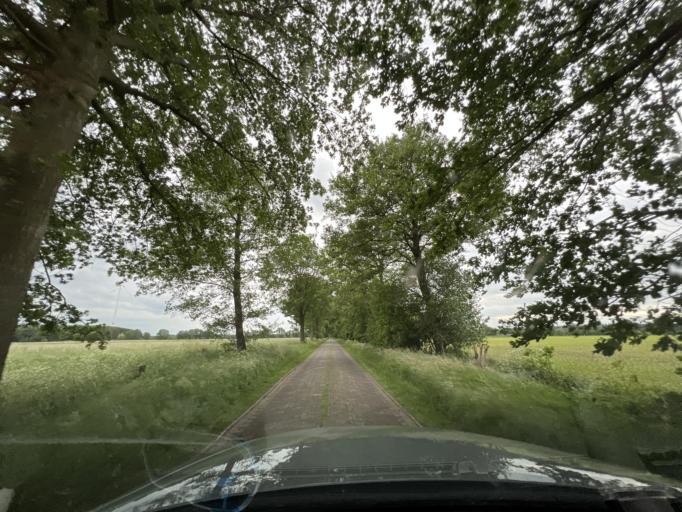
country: DE
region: Lower Saxony
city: Hatten
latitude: 53.0446
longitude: 8.3149
